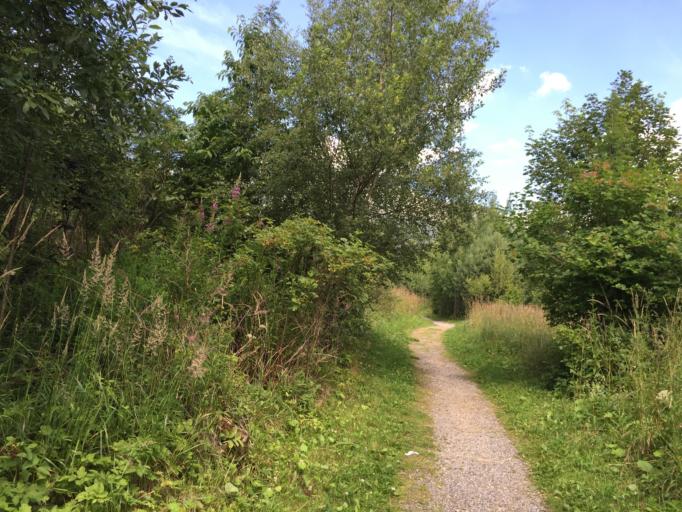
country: SK
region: Presovsky
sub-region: Okres Poprad
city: Vysoke Tatry
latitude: 49.1347
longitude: 20.2392
